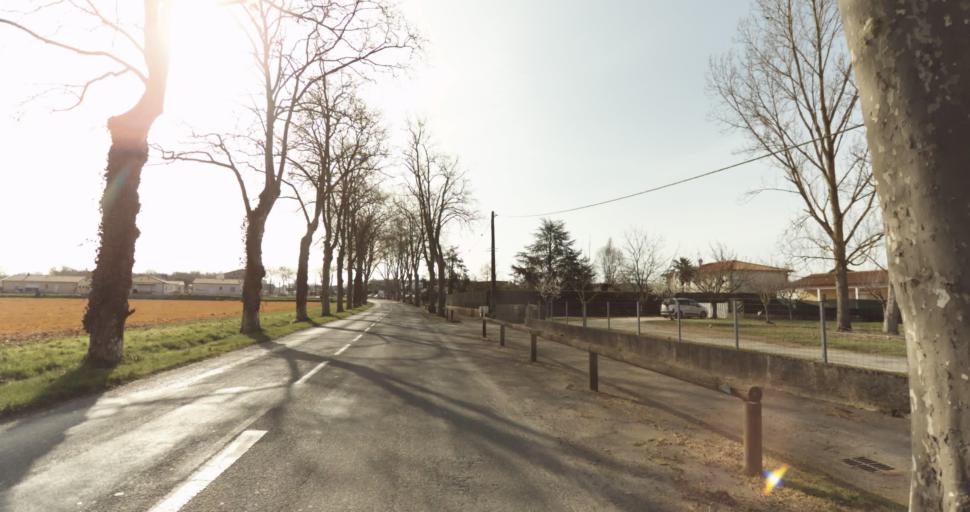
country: FR
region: Midi-Pyrenees
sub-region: Departement du Tarn
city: Saint-Sulpice-la-Pointe
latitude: 43.7627
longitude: 1.6969
